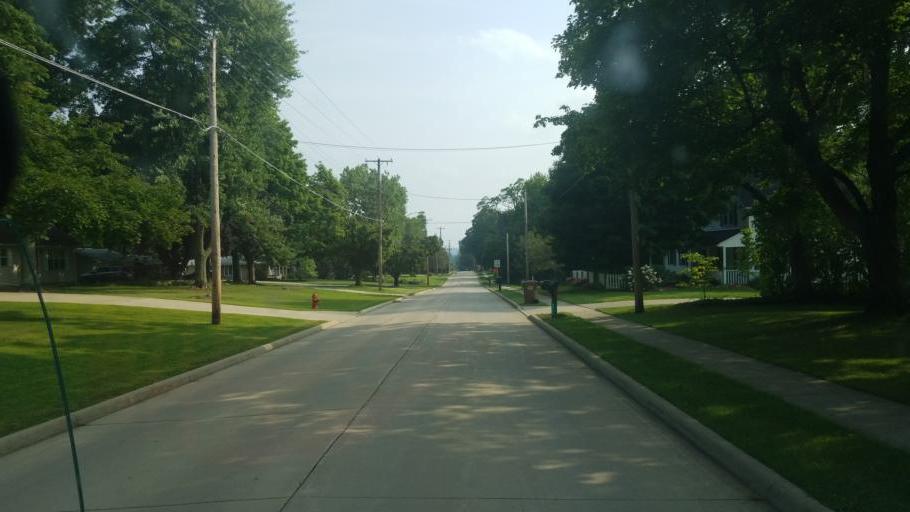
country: US
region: Ohio
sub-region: Medina County
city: Westfield Center
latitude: 41.0296
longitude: -81.9416
